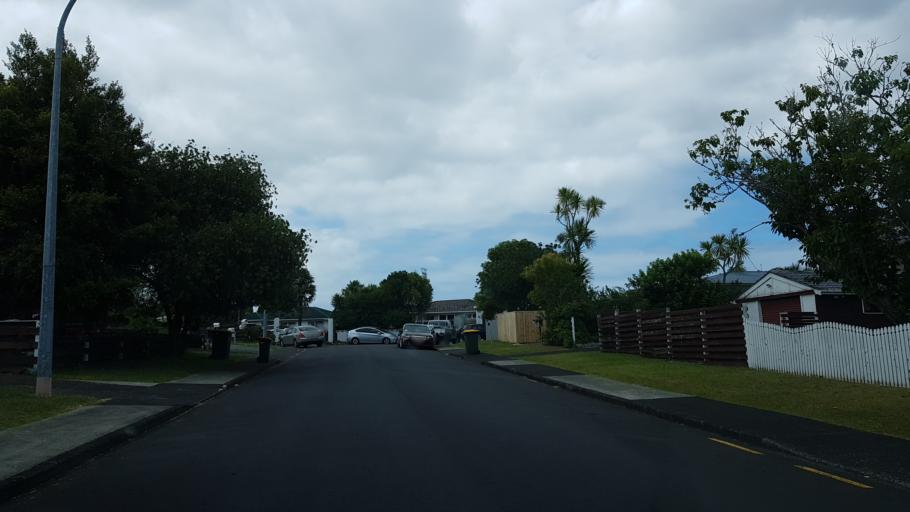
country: NZ
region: Auckland
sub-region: Auckland
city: North Shore
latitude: -36.7756
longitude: 174.7300
